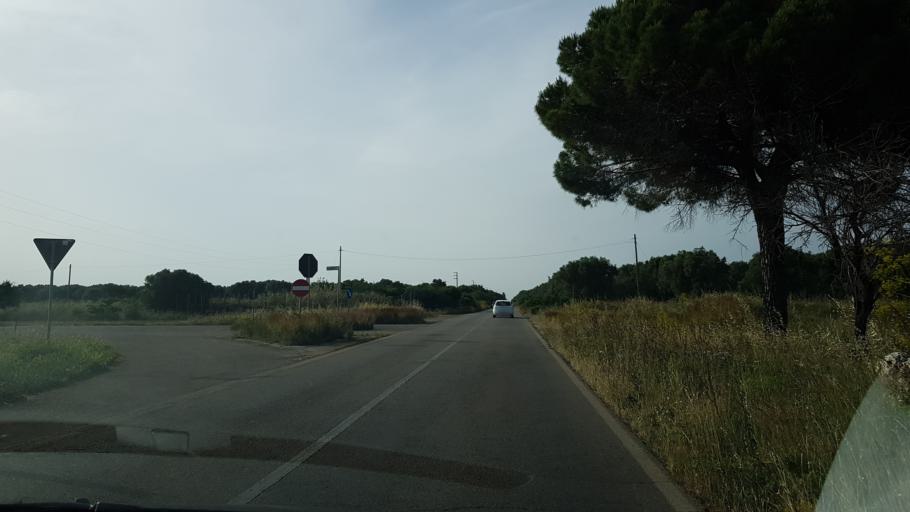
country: IT
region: Apulia
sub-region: Provincia di Brindisi
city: San Pancrazio Salentino
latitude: 40.3450
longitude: 17.8475
